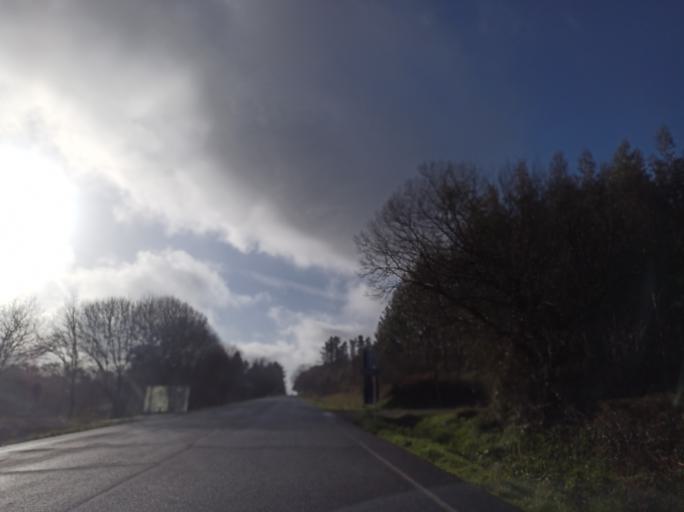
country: ES
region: Galicia
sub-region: Provincia da Coruna
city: Curtis
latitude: 43.0913
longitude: -8.0175
